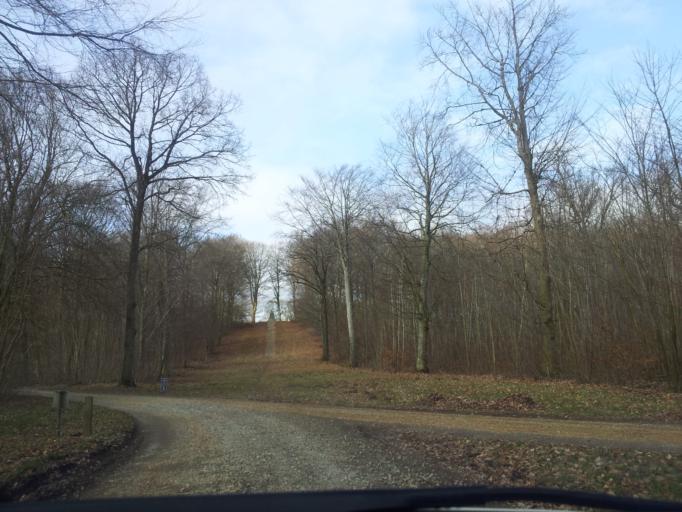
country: DK
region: South Denmark
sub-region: Vejen Kommune
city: Vejen
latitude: 55.4459
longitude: 9.1121
